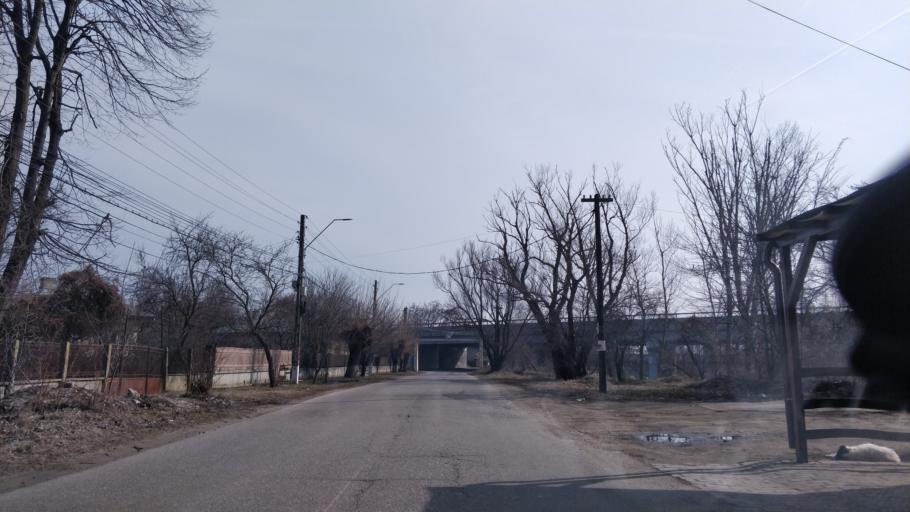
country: RO
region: Giurgiu
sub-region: Comuna Ulmi
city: Ulmi
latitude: 44.4692
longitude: 25.7685
